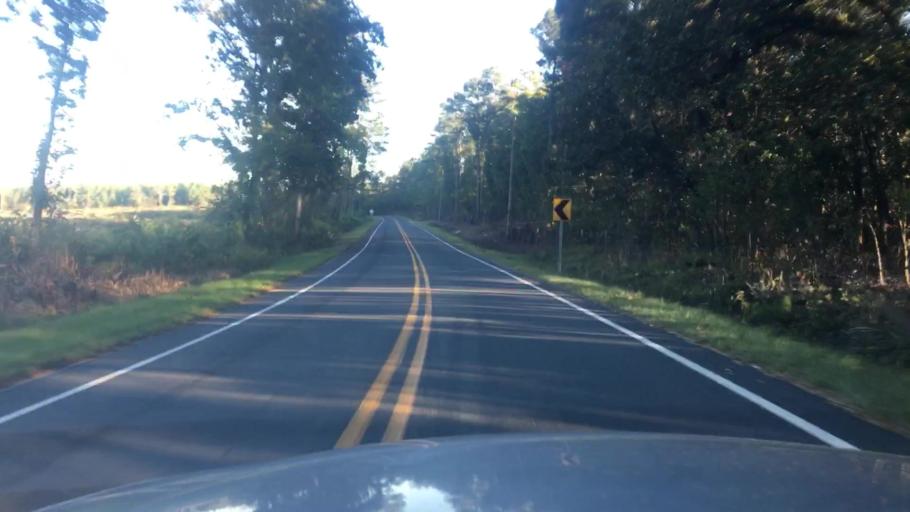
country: US
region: North Carolina
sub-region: Harnett County
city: Walkertown
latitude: 35.2884
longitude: -78.8694
